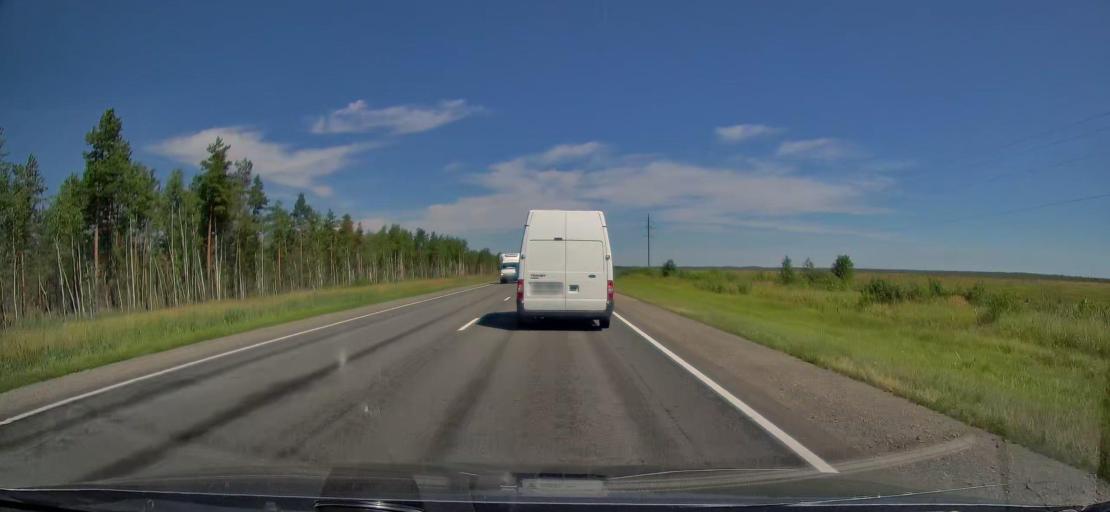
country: RU
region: Vologda
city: Khokhlovo
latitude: 58.9785
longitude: 37.3247
